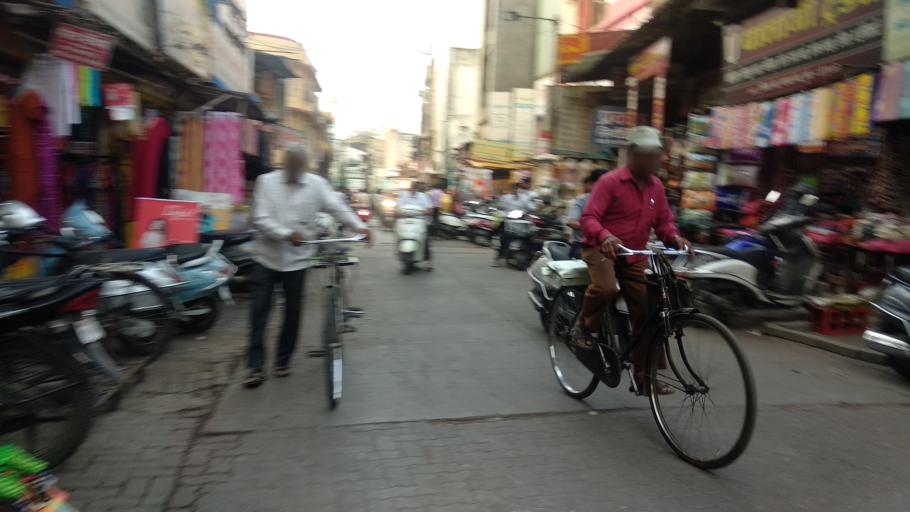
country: IN
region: Maharashtra
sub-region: Pune Division
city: Pune
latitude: 18.5152
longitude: 73.8600
